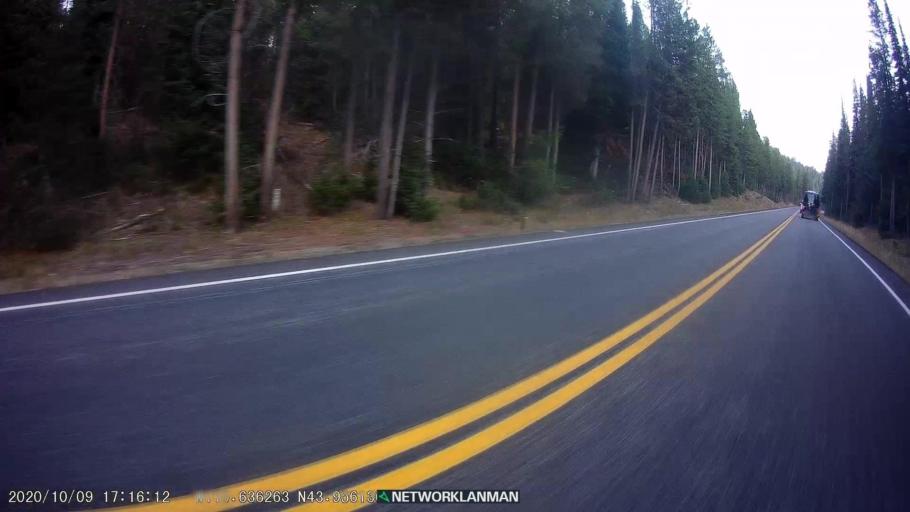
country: US
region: Wyoming
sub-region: Teton County
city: Moose Wilson Road
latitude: 43.9561
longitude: -110.6363
